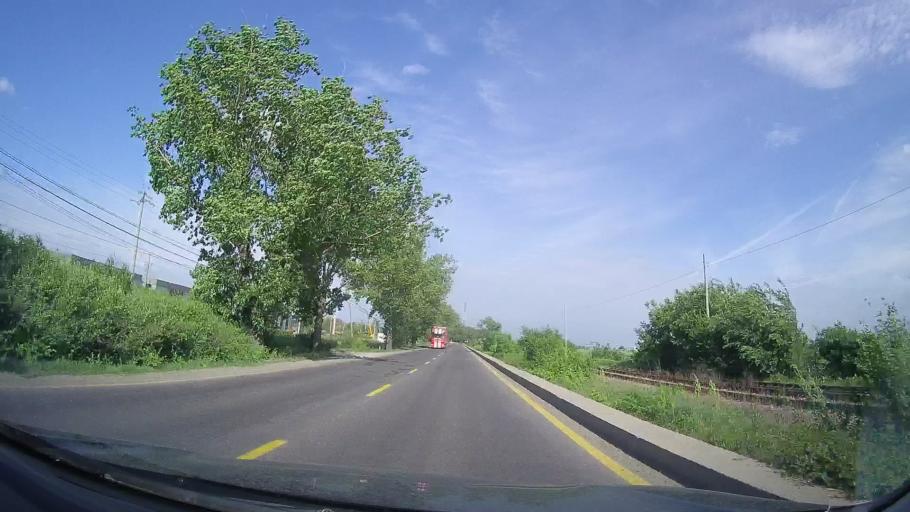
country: RO
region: Ilfov
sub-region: Comuna Magurele
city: Magurele
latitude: 44.3611
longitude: 26.0305
